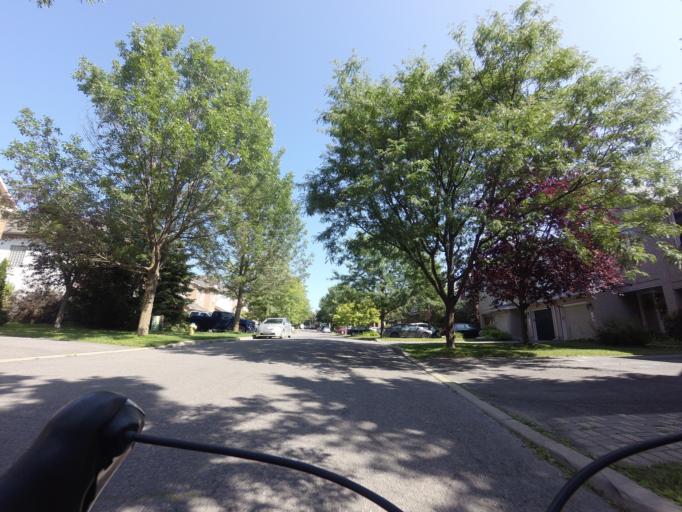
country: CA
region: Ontario
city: Bells Corners
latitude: 45.2776
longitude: -75.8526
